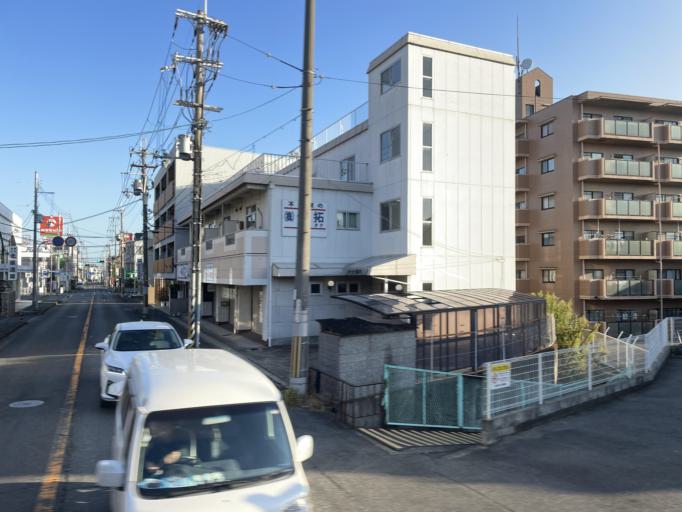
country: JP
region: Osaka
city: Kashihara
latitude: 34.5711
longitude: 135.5994
